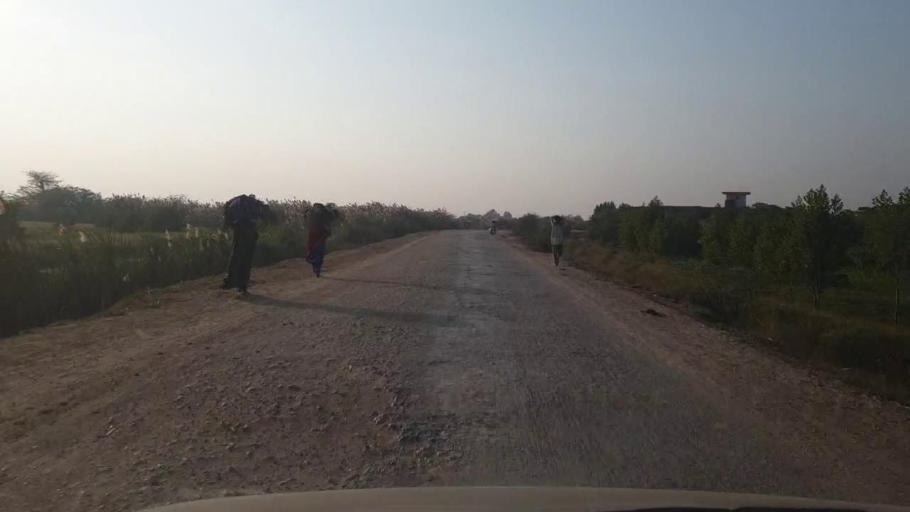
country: PK
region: Sindh
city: Mirwah Gorchani
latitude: 25.3719
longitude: 69.1282
